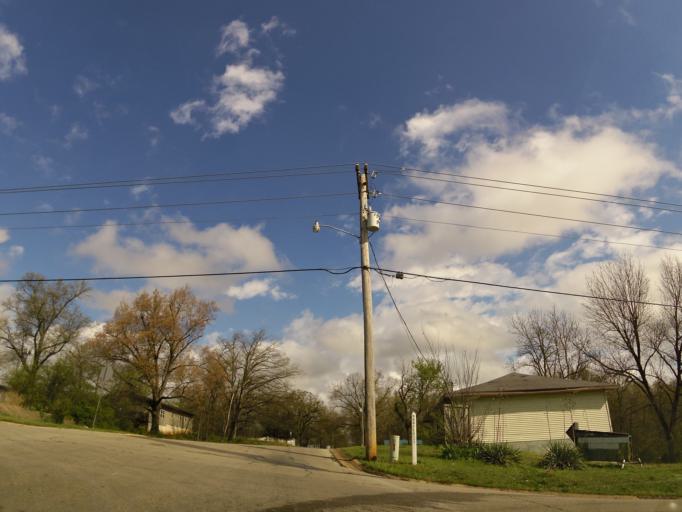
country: US
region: Missouri
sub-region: Butler County
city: Poplar Bluff
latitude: 36.7663
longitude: -90.3949
